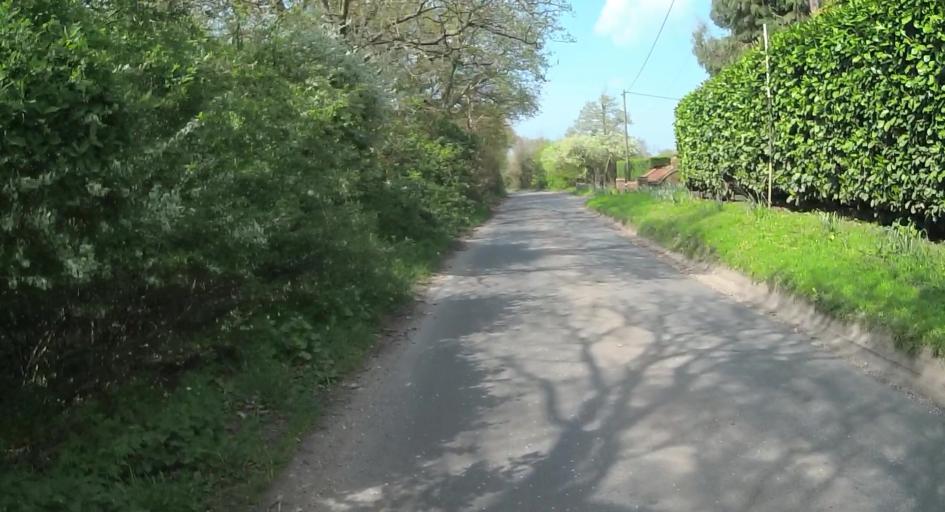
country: GB
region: England
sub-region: Hampshire
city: Tadley
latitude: 51.3798
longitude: -1.1277
